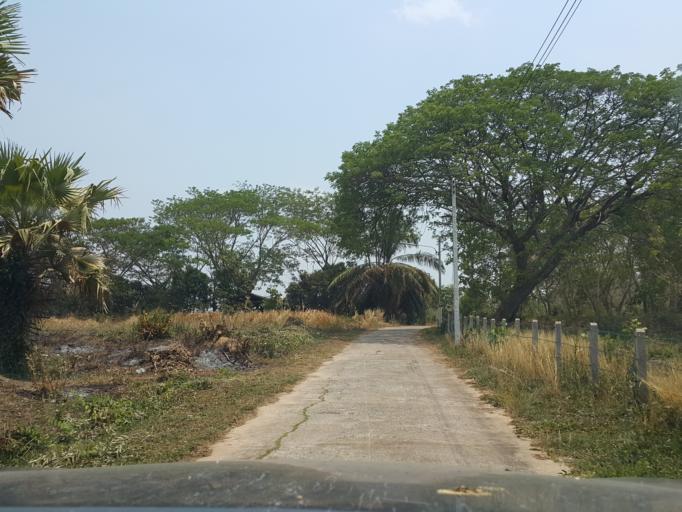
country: TH
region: Lampang
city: Mae Phrik
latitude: 17.5711
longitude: 99.0862
